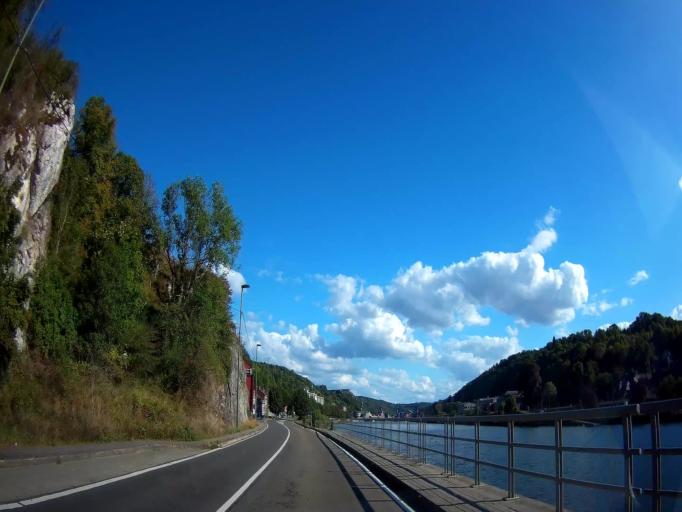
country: BE
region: Wallonia
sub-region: Province de Namur
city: Dinant
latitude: 50.2743
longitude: 4.8999
